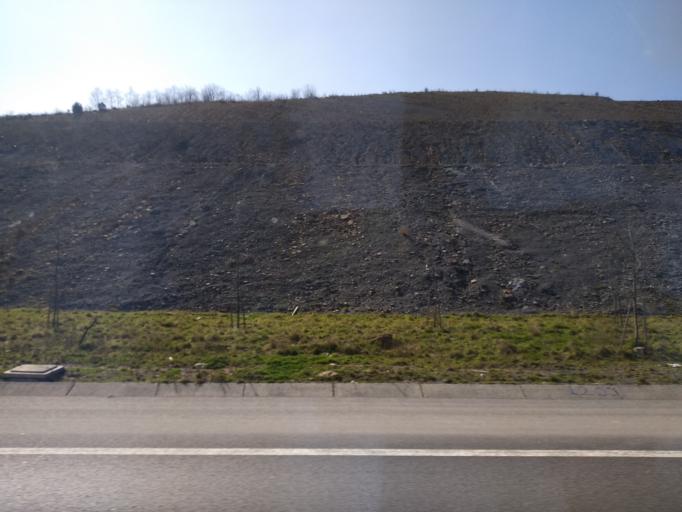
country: TR
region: Istanbul
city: Mahmut Sevket Pasa
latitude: 41.1573
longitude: 29.2641
